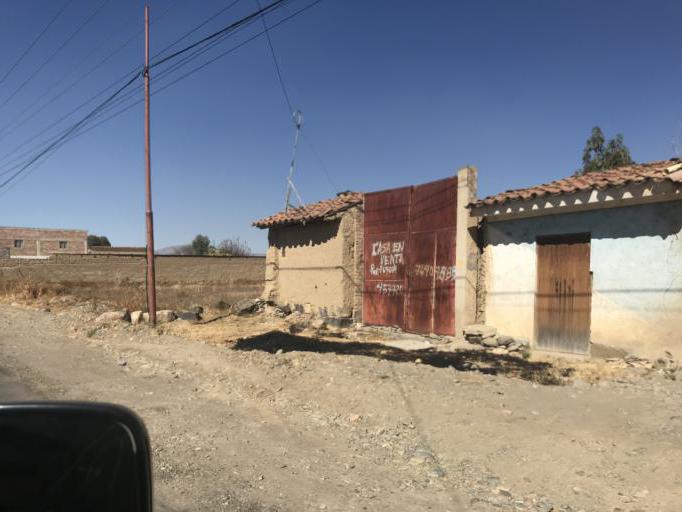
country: BO
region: Cochabamba
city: Cliza
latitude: -17.5643
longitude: -65.8847
